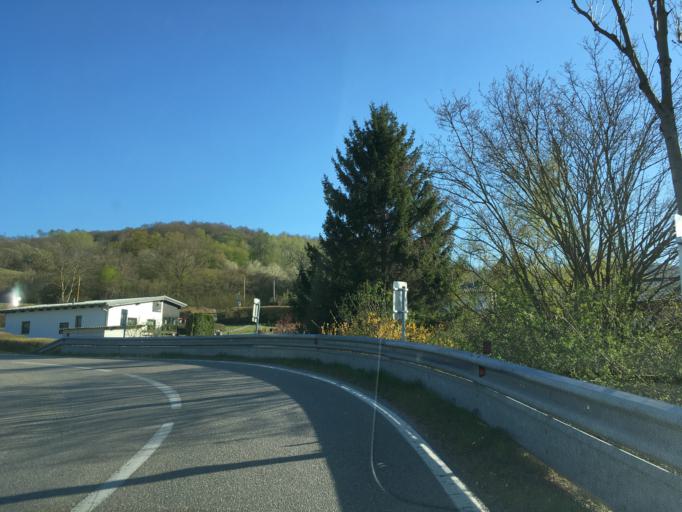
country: AT
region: Lower Austria
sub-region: Politischer Bezirk Tulln
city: Konigstetten
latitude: 48.3001
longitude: 16.1592
